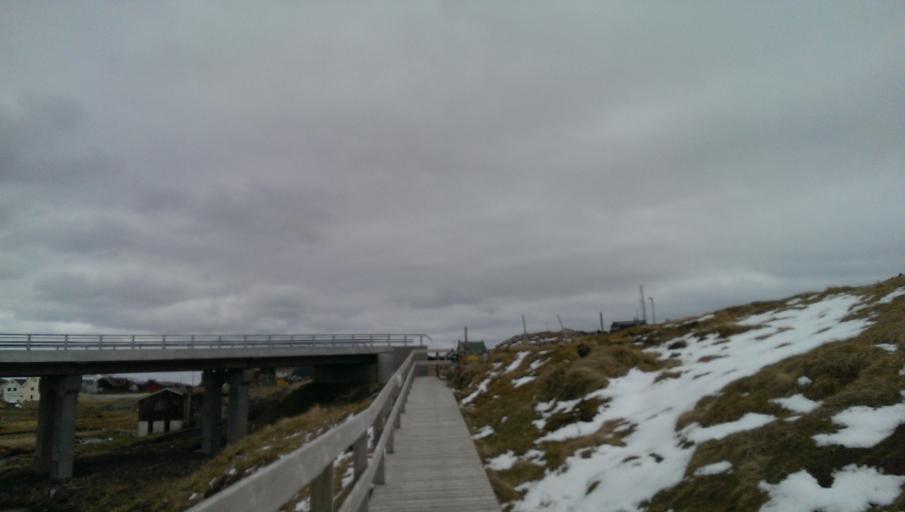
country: FO
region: Streymoy
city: Hoyvik
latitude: 62.0321
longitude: -6.7977
